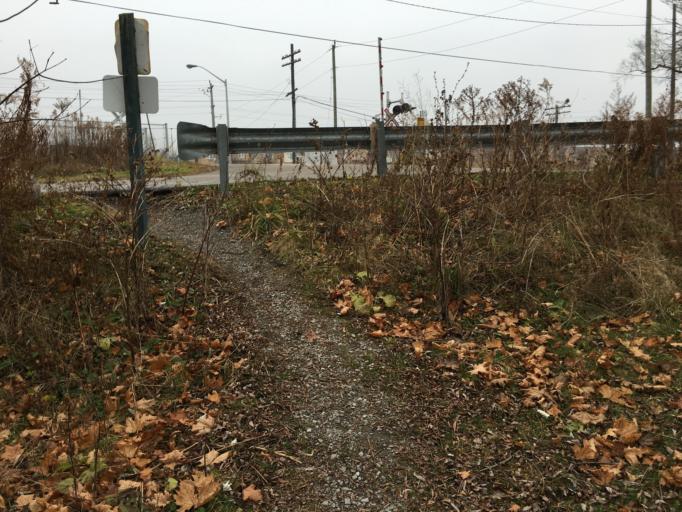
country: CA
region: Ontario
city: Ajax
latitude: 43.7807
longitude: -79.1293
